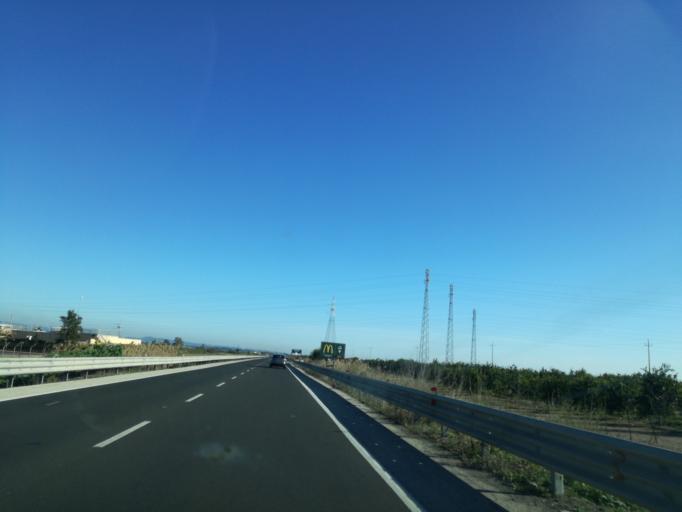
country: IT
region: Sicily
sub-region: Catania
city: Motta Sant'Anastasia
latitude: 37.4195
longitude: 14.9139
